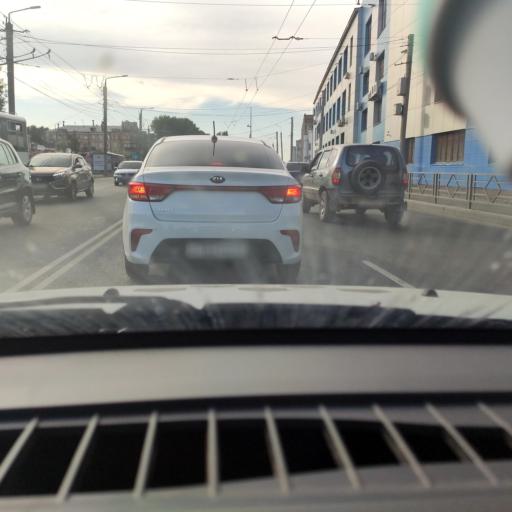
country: RU
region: Kirov
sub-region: Kirovo-Chepetskiy Rayon
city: Kirov
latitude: 58.6237
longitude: 49.6494
